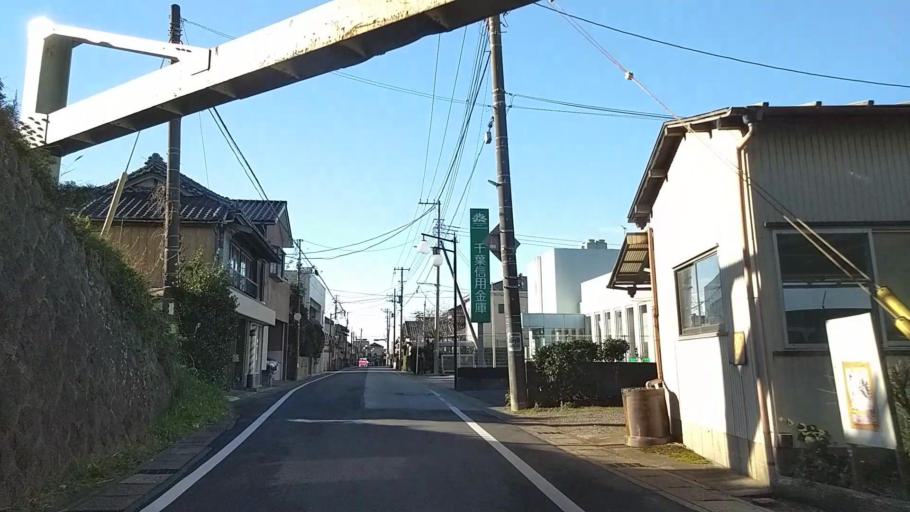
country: JP
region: Chiba
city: Futtsu
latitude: 35.2844
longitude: 139.8577
